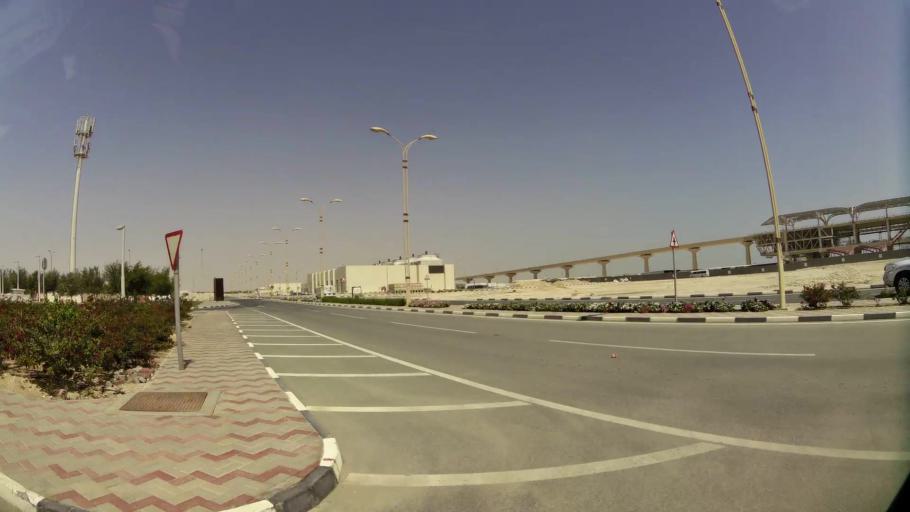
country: QA
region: Baladiyat Umm Salal
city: Umm Salal Muhammad
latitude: 25.3813
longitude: 51.4911
